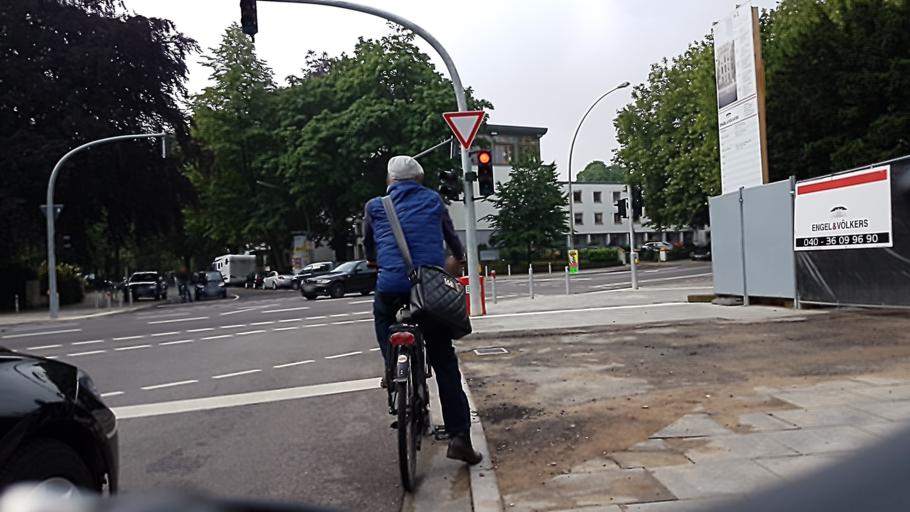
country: DE
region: Hamburg
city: Winterhude
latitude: 53.5856
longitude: 9.9995
